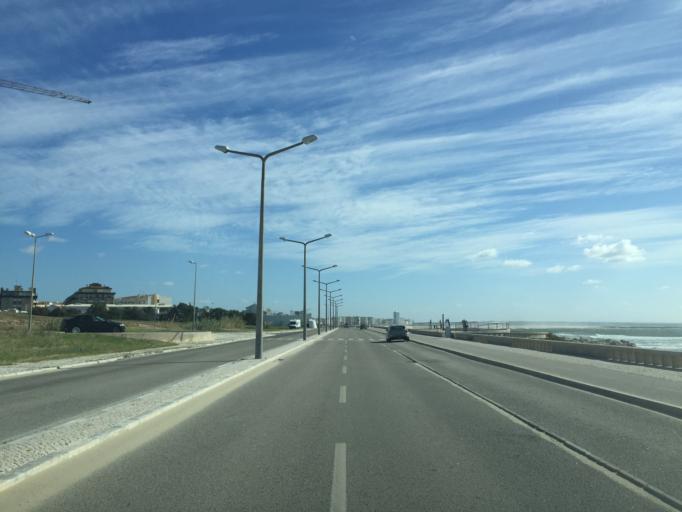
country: PT
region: Coimbra
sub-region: Figueira da Foz
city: Buarcos
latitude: 40.1683
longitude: -8.8869
